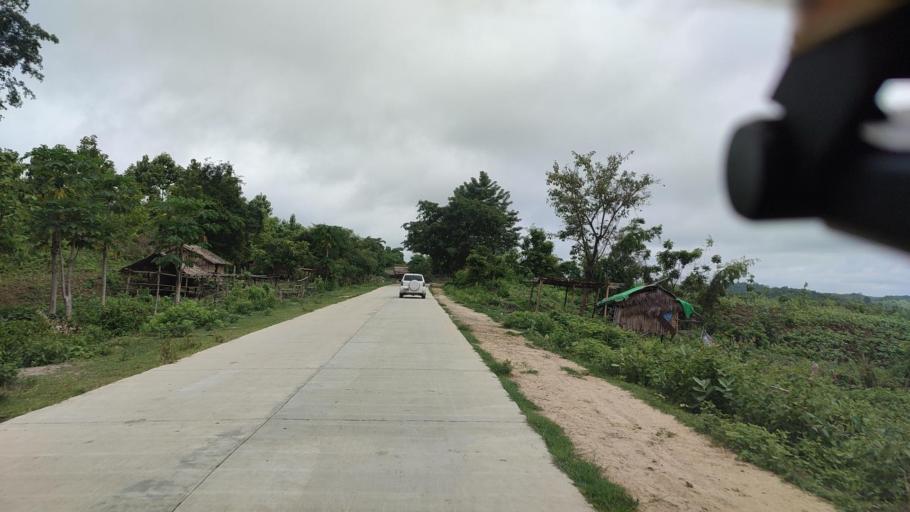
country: MM
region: Magway
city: Taungdwingyi
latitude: 20.0237
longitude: 95.7930
